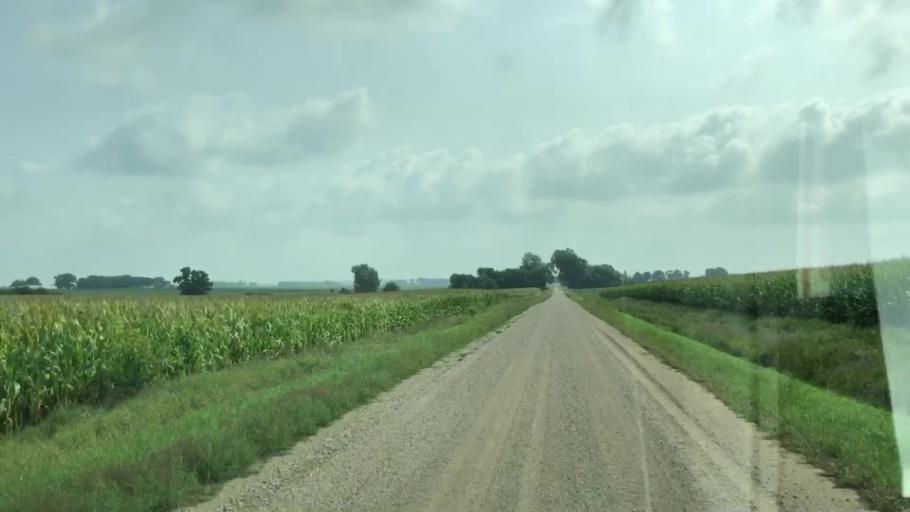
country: US
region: Iowa
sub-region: O'Brien County
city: Sheldon
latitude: 43.2004
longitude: -95.8954
